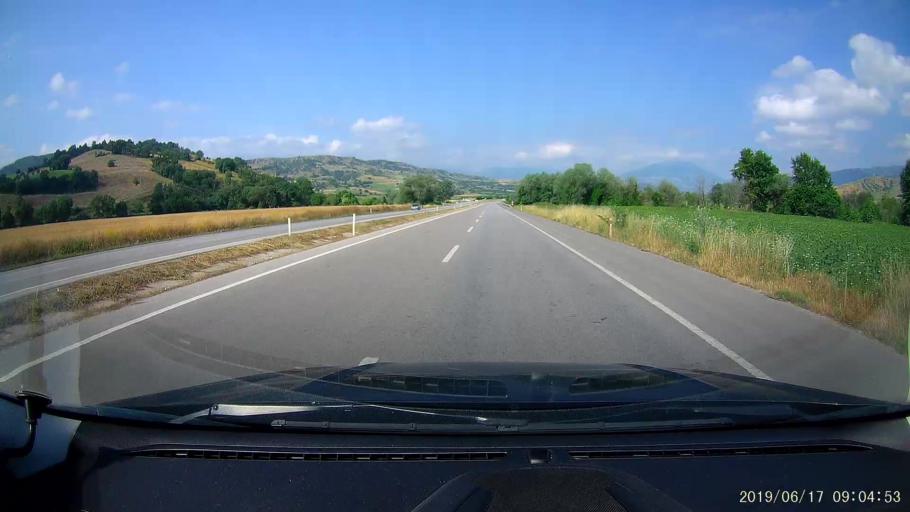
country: TR
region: Amasya
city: Tasova
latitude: 40.7414
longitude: 36.2782
